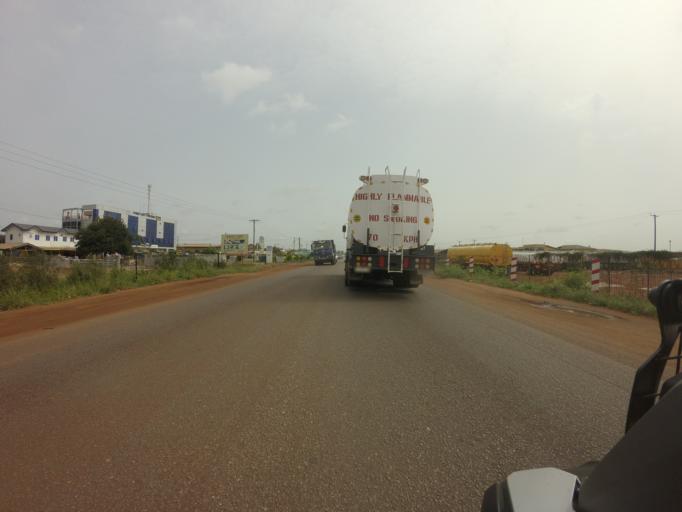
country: GH
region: Greater Accra
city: Tema
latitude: 5.7211
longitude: 0.0188
